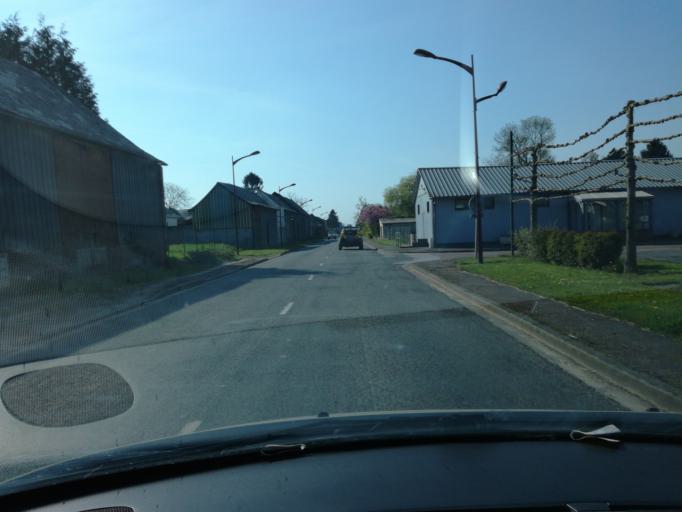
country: FR
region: Picardie
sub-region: Departement de la Somme
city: Hornoy-le-Bourg
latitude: 49.8262
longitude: 1.9413
